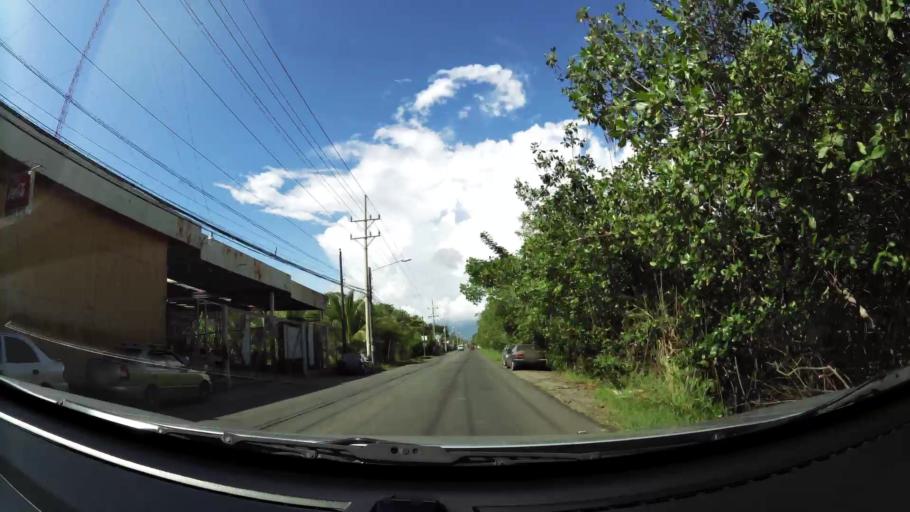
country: CR
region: Puntarenas
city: Quepos
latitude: 9.4383
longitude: -84.1645
